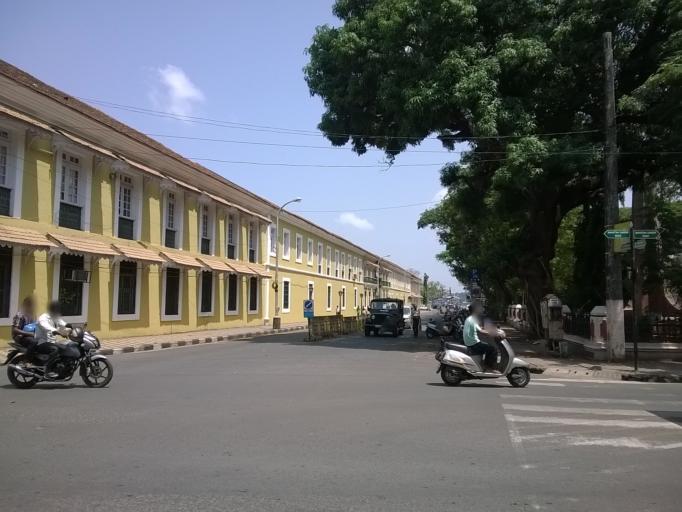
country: IN
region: Goa
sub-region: North Goa
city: Panaji
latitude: 15.4995
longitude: 73.8262
